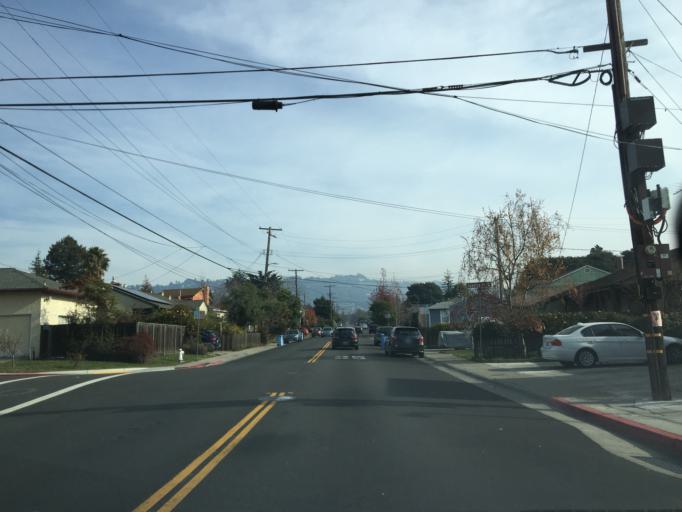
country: US
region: California
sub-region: Alameda County
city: Berkeley
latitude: 37.8762
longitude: -122.2870
